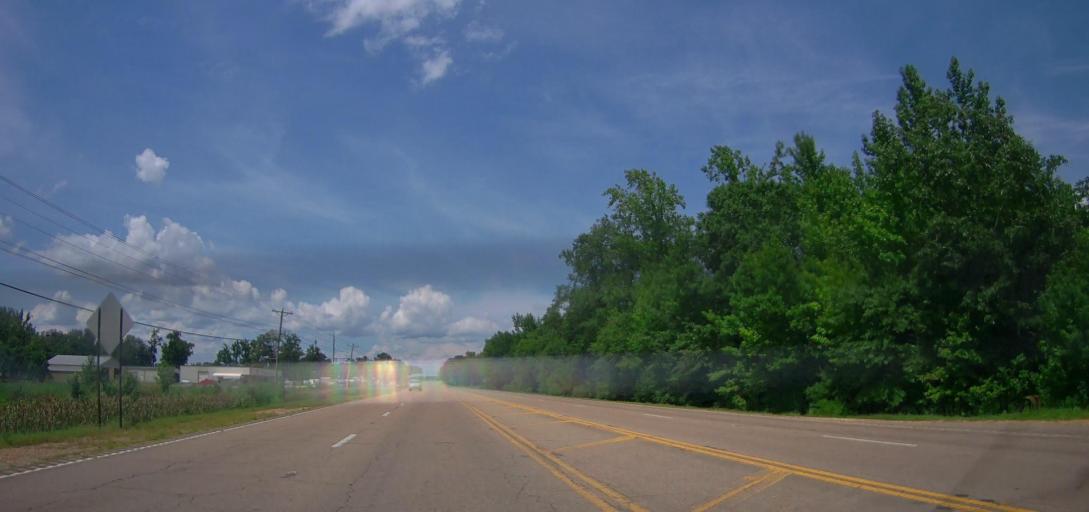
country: US
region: Mississippi
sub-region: Lee County
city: Shannon
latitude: 34.1529
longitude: -88.7195
